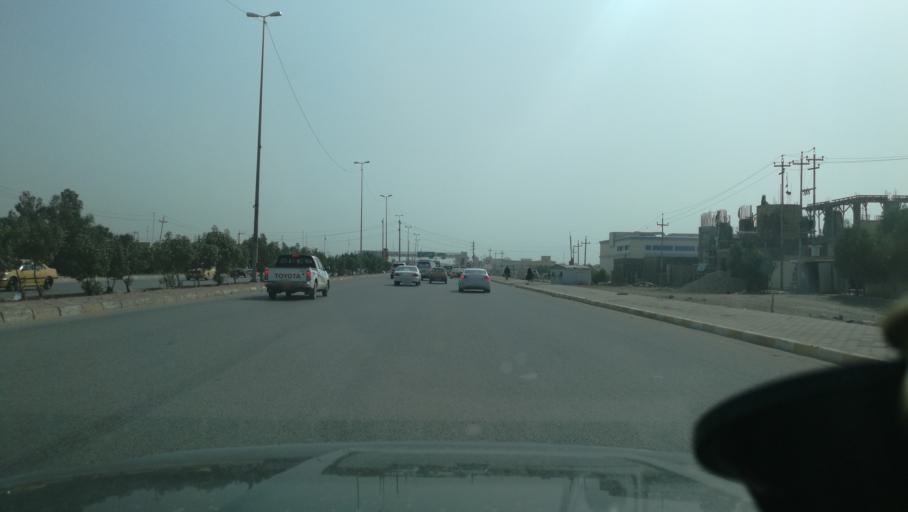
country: IQ
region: Dhi Qar
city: An Nasiriyah
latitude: 31.0618
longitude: 46.2482
